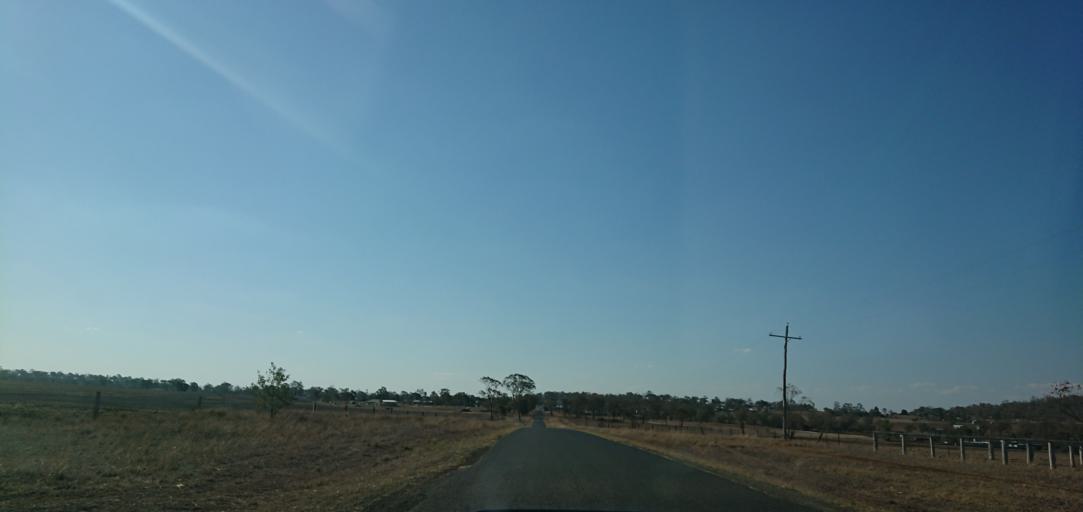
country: AU
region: Queensland
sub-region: Toowoomba
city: Westbrook
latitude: -27.6909
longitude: 151.7149
